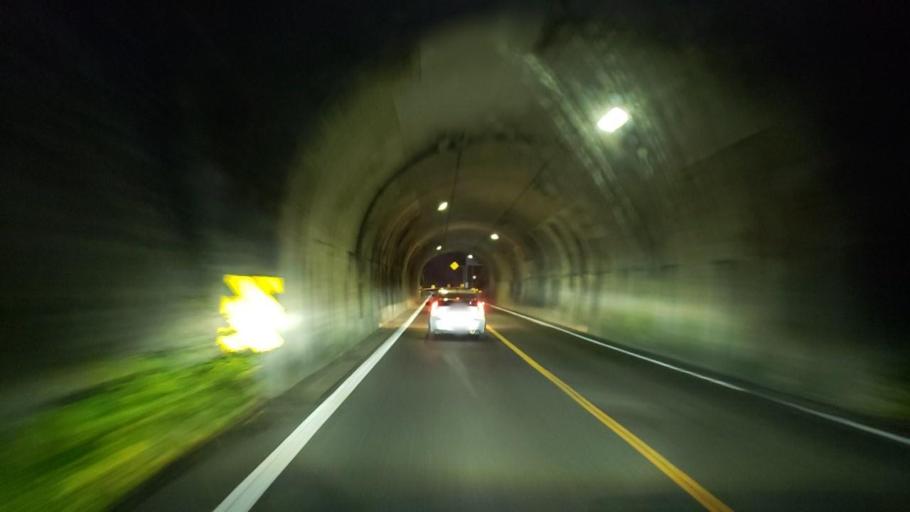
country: JP
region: Tokushima
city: Ishii
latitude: 34.2064
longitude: 134.4381
